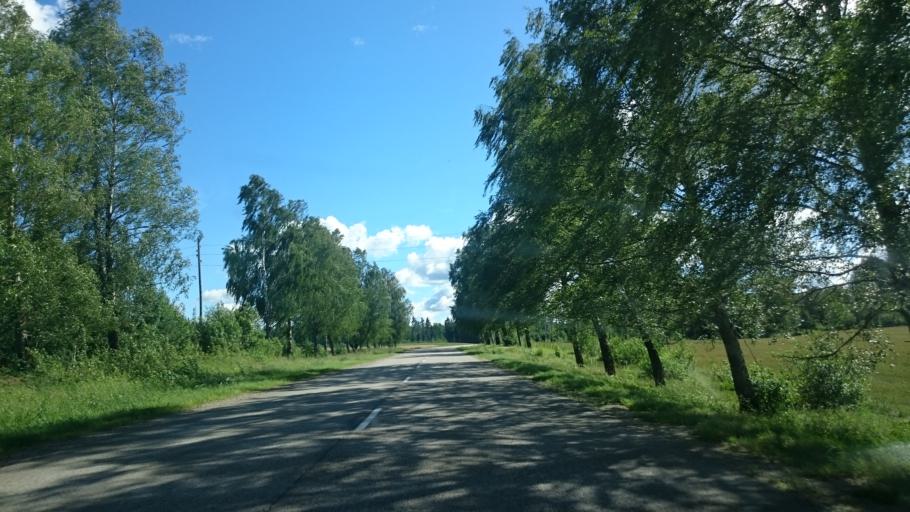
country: LV
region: Kuldigas Rajons
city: Kuldiga
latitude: 56.8964
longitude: 21.8882
